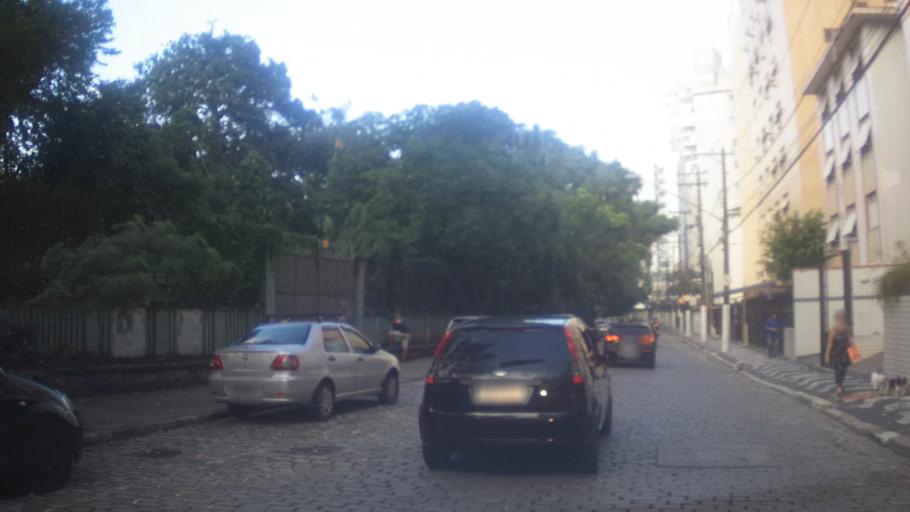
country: BR
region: Sao Paulo
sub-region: Santos
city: Santos
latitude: -23.9669
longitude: -46.3506
